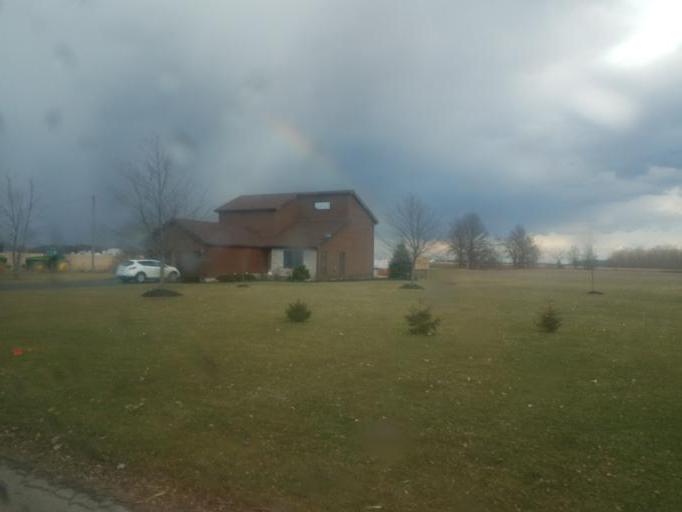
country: US
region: Ohio
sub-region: Marion County
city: Prospect
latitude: 40.4758
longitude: -83.1176
